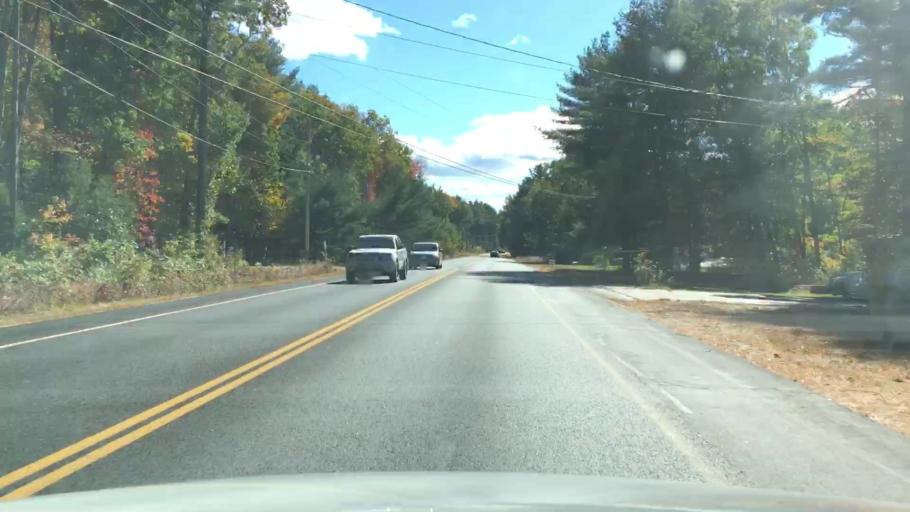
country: US
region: Maine
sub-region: York County
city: South Sanford
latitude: 43.4319
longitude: -70.7336
